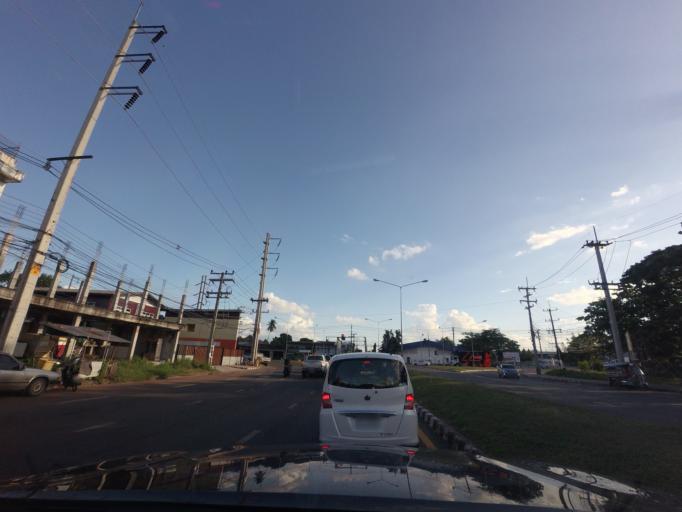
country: TH
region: Changwat Udon Thani
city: Nong Han
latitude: 17.3627
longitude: 103.1775
